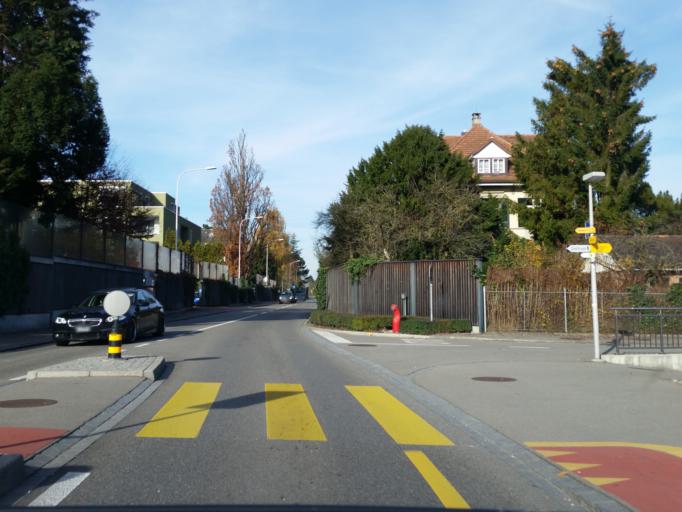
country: CH
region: Thurgau
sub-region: Kreuzlingen District
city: Kreuzlingen
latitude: 47.6501
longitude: 9.1802
